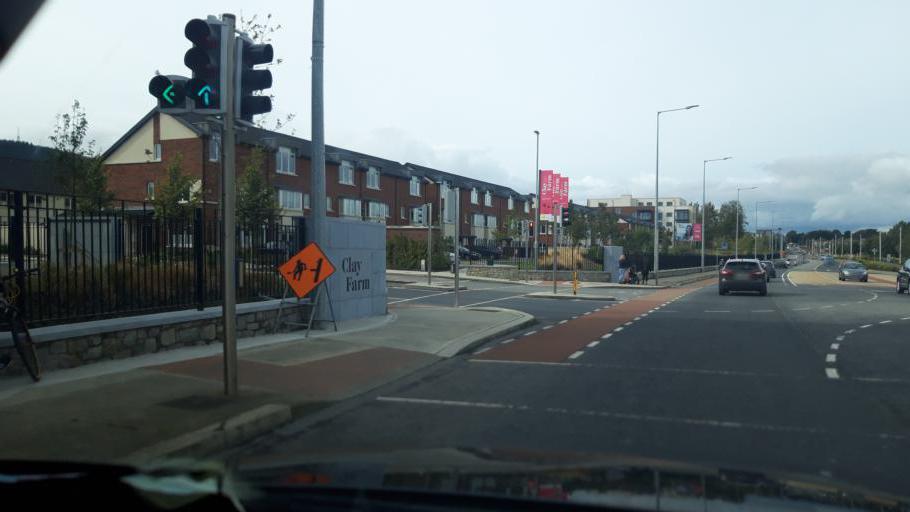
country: IE
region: Leinster
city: Foxrock
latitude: 53.2582
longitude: -6.1988
